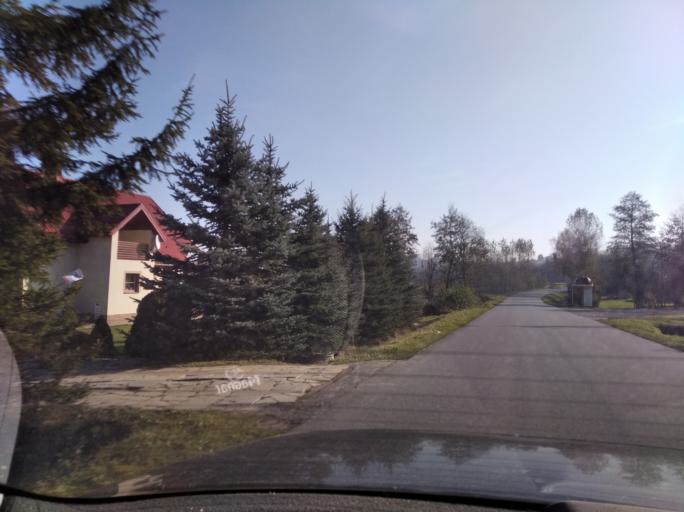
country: PL
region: Subcarpathian Voivodeship
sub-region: Powiat ropczycko-sedziszowski
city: Wielopole Skrzynskie
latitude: 49.9481
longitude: 21.5988
